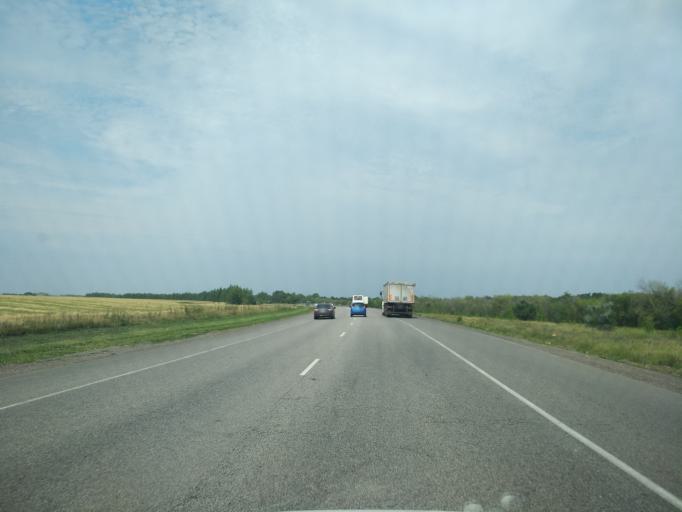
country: RU
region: Voronezj
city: Novaya Usman'
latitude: 51.6996
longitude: 39.4281
